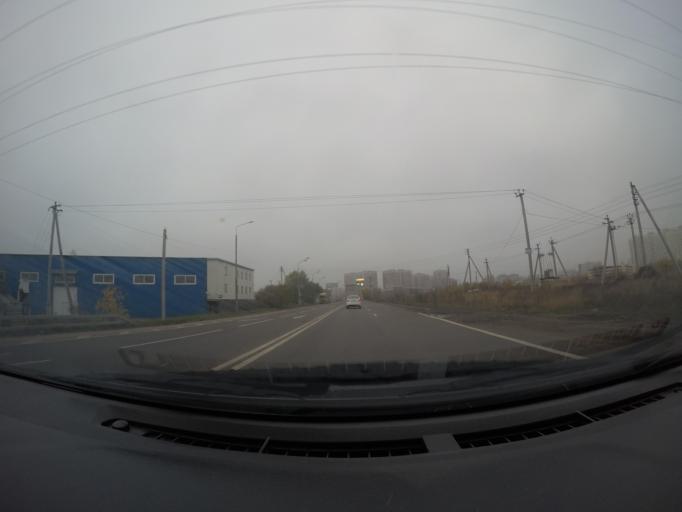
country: RU
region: Moskovskaya
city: Shcherbinka
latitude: 55.4971
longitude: 37.5755
